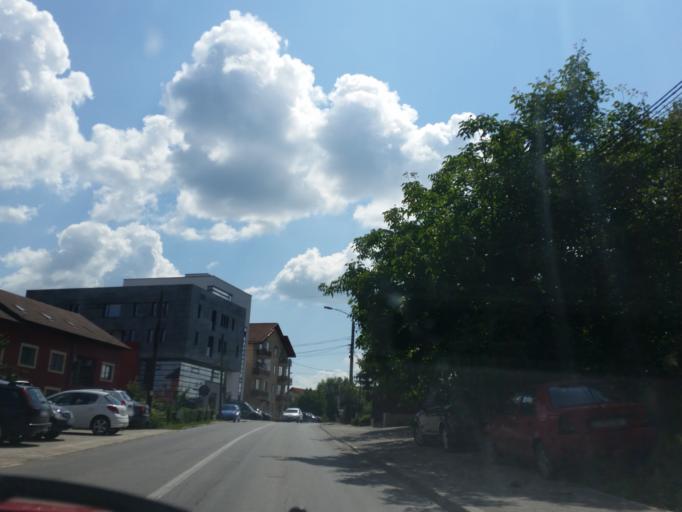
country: RO
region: Cluj
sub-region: Municipiul Cluj-Napoca
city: Cluj-Napoca
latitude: 46.7513
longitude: 23.6093
